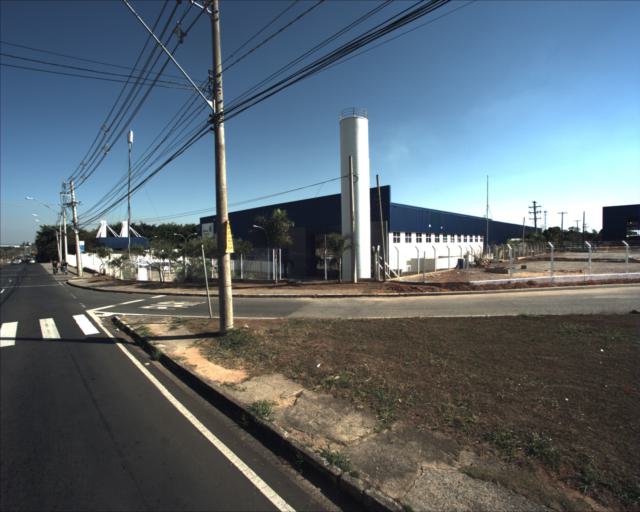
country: BR
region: Sao Paulo
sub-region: Sorocaba
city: Sorocaba
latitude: -23.4400
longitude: -47.4166
